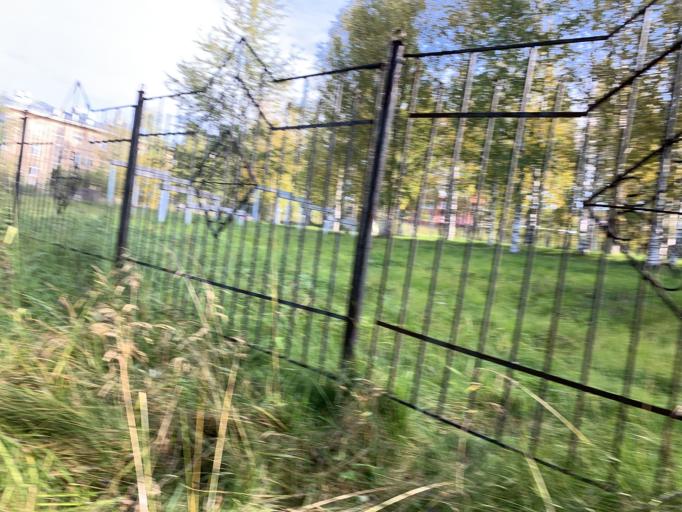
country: RU
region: Perm
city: Gubakha
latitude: 58.8373
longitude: 57.5587
